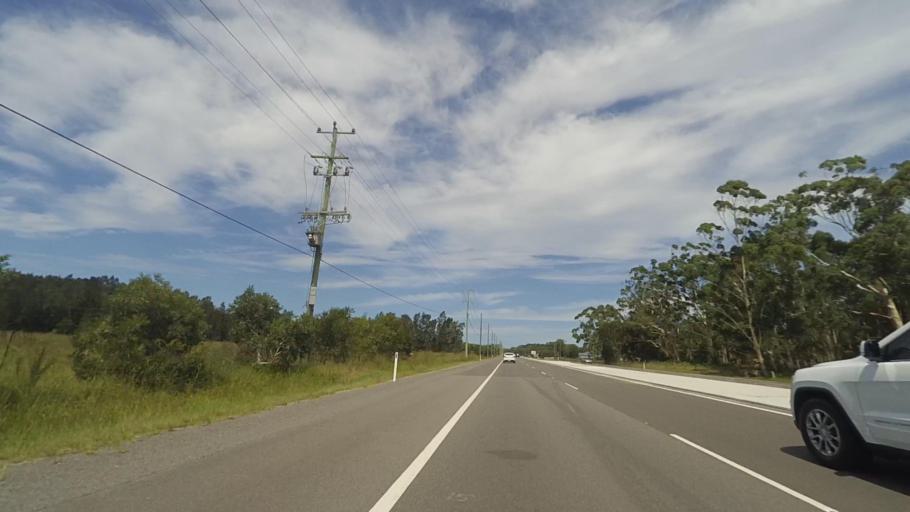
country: AU
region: New South Wales
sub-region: Port Stephens Shire
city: Anna Bay
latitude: -32.7675
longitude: 152.0225
